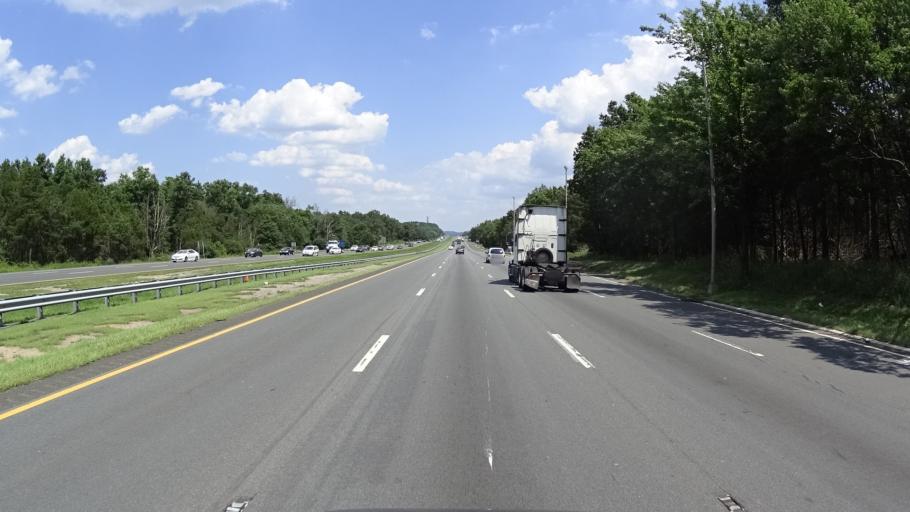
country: US
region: New Jersey
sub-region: Hunterdon County
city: Whitehouse Station
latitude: 40.6440
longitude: -74.7107
